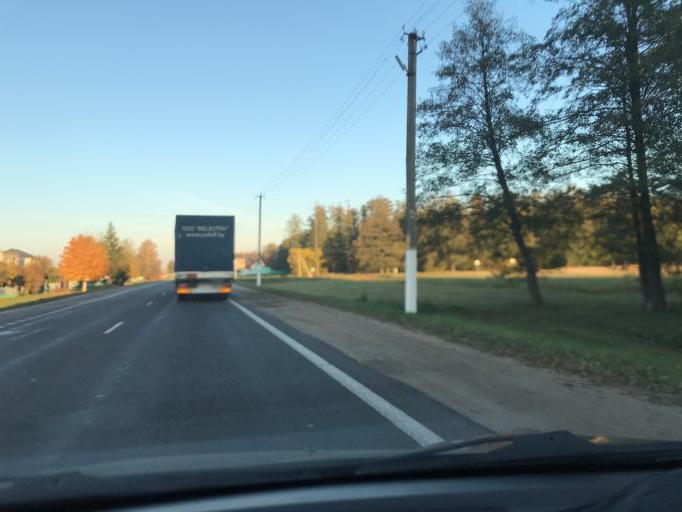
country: BY
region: Minsk
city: Staryya Darohi
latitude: 53.0342
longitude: 28.2775
